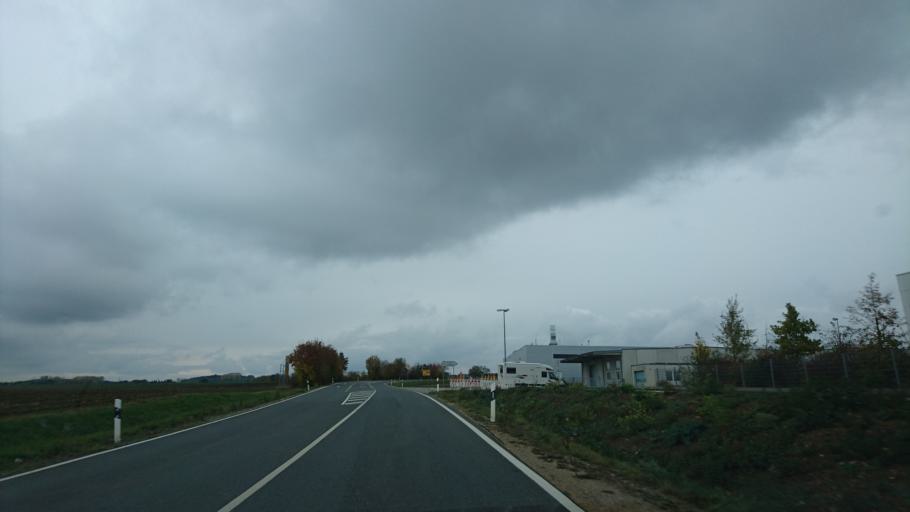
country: DE
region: Bavaria
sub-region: Regierungsbezirk Mittelfranken
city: Hilpoltstein
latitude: 49.1580
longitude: 11.2565
